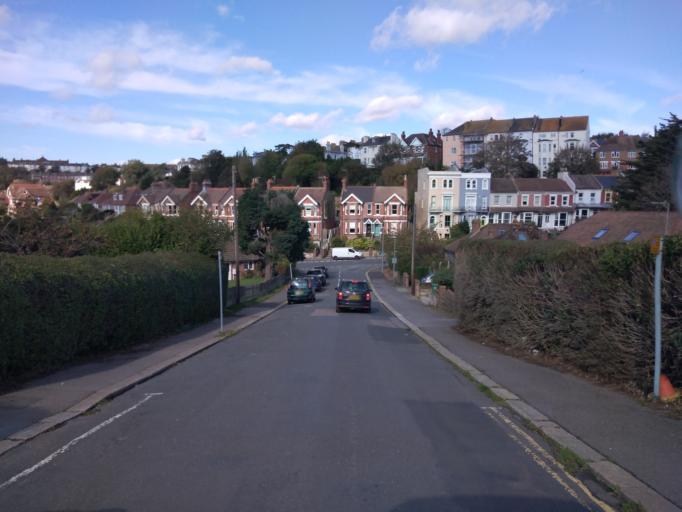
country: GB
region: England
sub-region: East Sussex
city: Hastings
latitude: 50.8631
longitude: 0.6030
